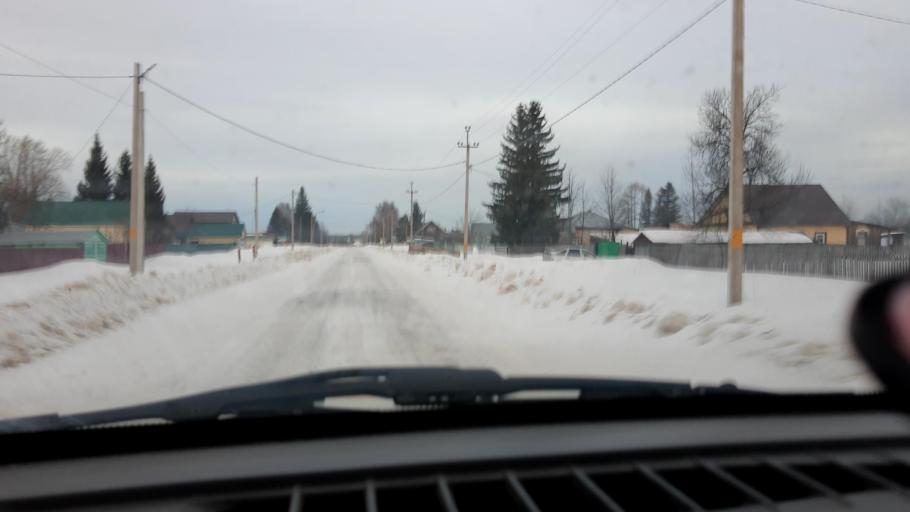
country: RU
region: Bashkortostan
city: Urman
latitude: 54.8686
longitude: 56.8662
